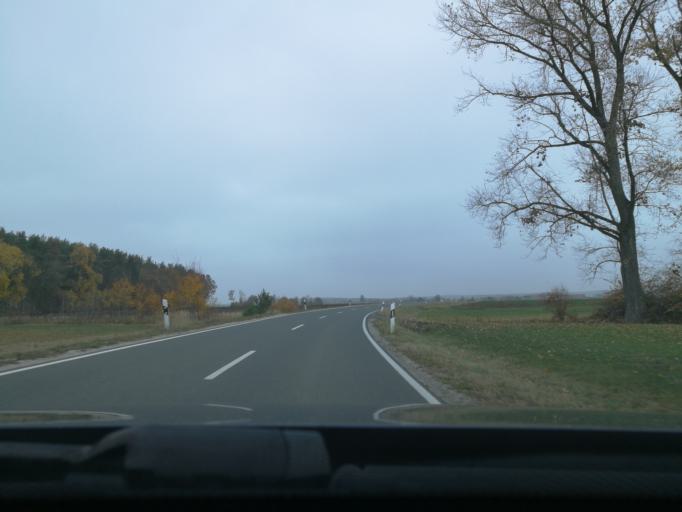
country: DE
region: Bavaria
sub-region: Regierungsbezirk Mittelfranken
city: Puschendorf
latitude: 49.5632
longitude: 10.8351
